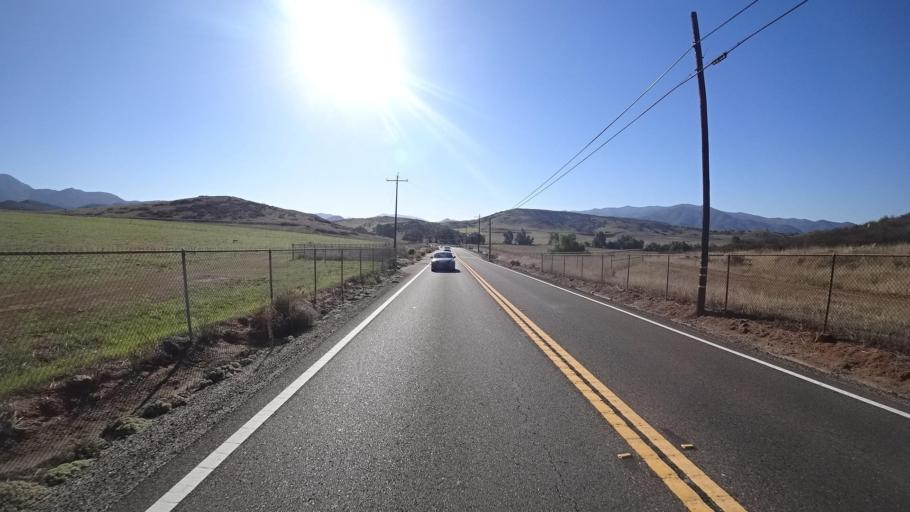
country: US
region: California
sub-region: San Diego County
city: Jamul
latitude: 32.6872
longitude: -116.8511
